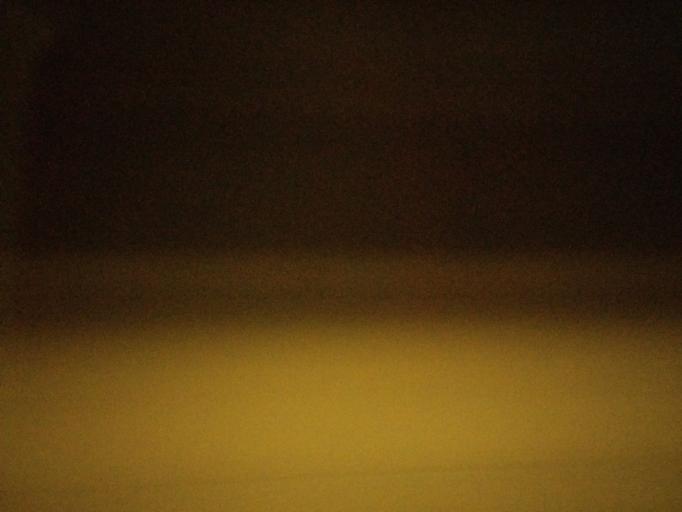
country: JP
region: Shiga Prefecture
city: Nagahama
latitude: 35.3666
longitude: 136.3790
